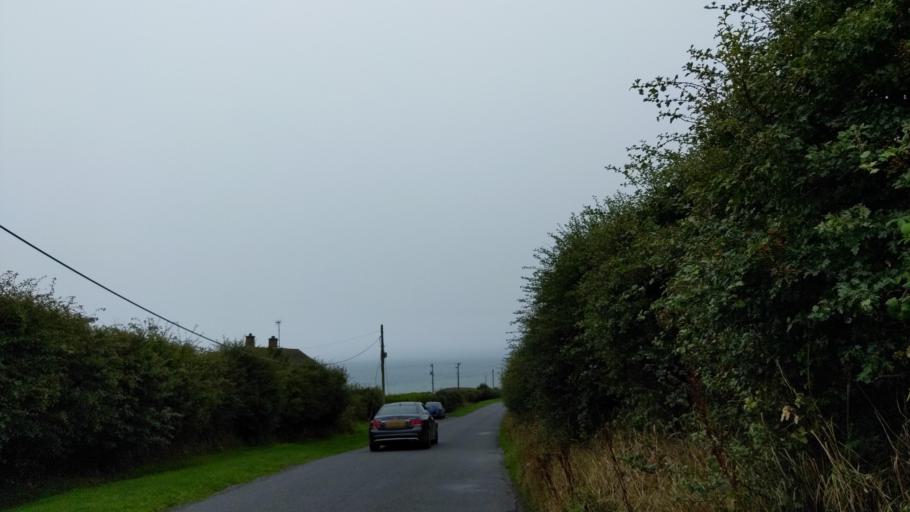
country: IE
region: Leinster
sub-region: Lu
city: Clogherhead
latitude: 53.7933
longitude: -6.2285
